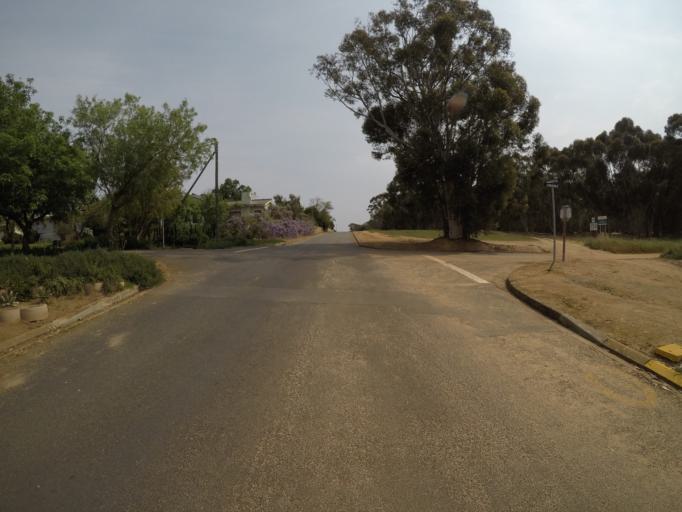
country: ZA
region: Western Cape
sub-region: West Coast District Municipality
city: Malmesbury
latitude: -33.4594
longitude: 18.7386
